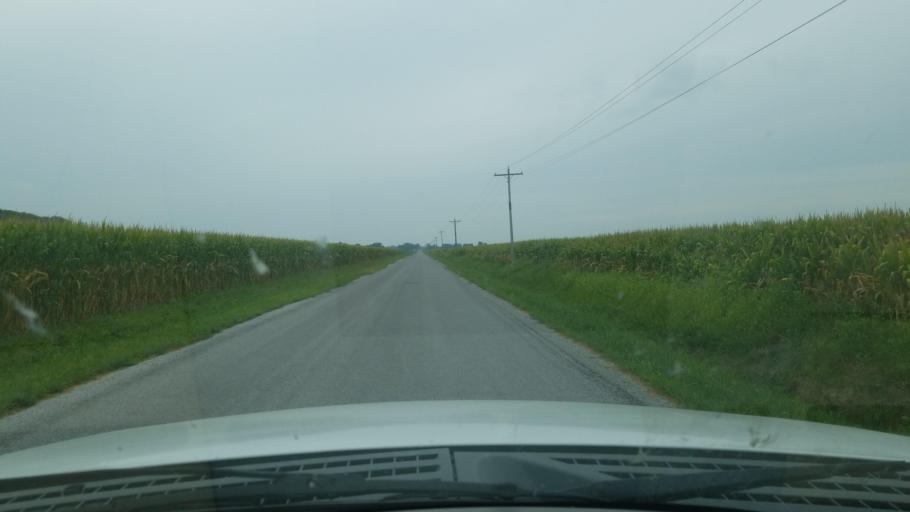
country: US
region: Illinois
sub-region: Saline County
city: Eldorado
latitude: 37.8670
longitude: -88.4665
